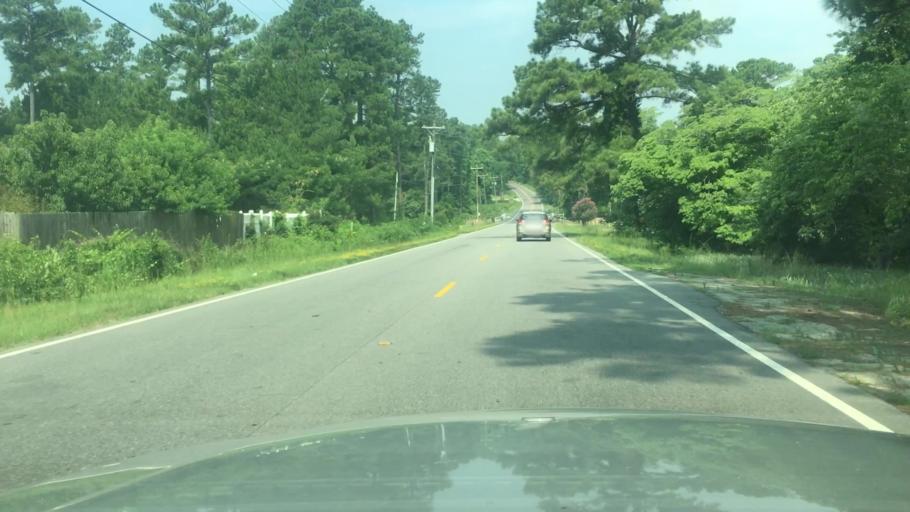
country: US
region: North Carolina
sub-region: Cumberland County
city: Hope Mills
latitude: 35.0014
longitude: -78.9579
